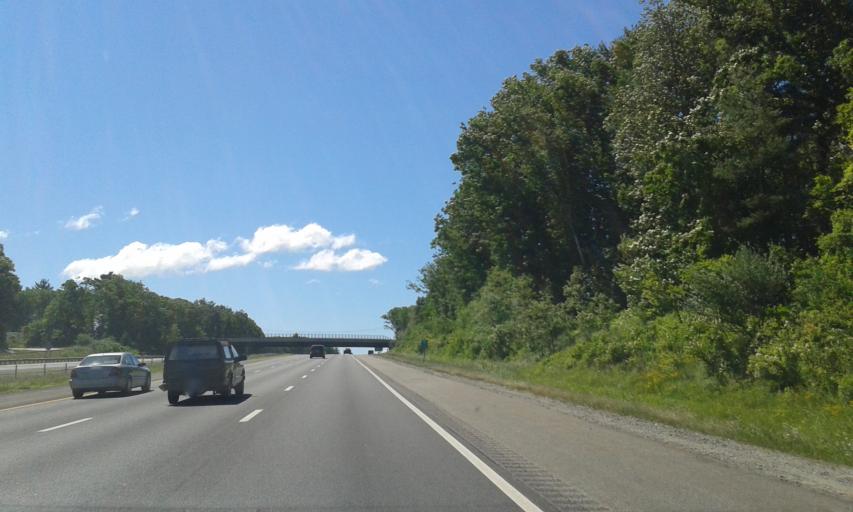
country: US
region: Massachusetts
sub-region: Middlesex County
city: Billerica
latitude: 42.5460
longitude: -71.2863
